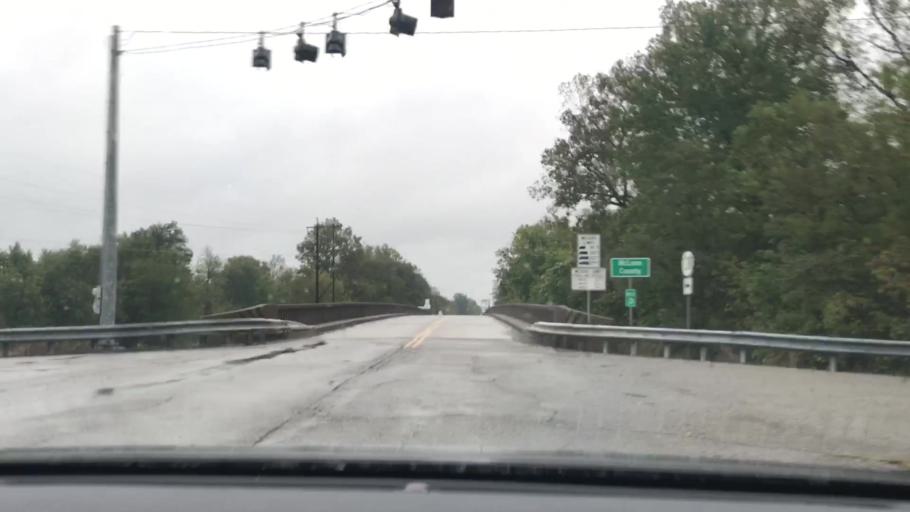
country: US
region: Kentucky
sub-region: McLean County
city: Calhoun
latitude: 37.5264
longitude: -87.3551
